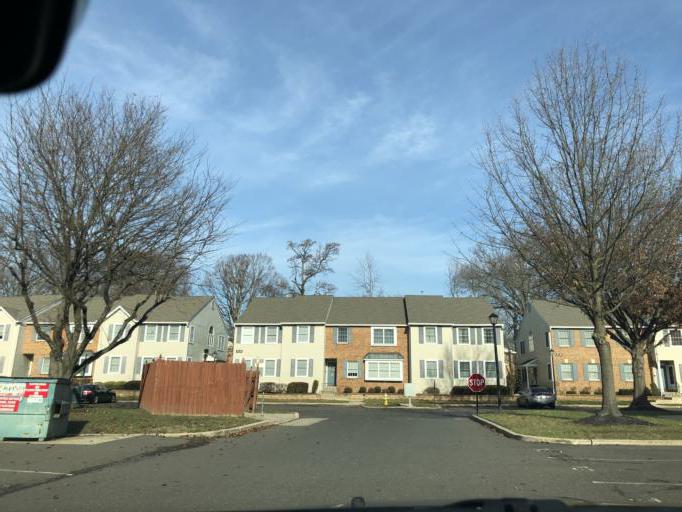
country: US
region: New Jersey
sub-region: Burlington County
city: Moorestown-Lenola
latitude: 39.9600
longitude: -74.9774
